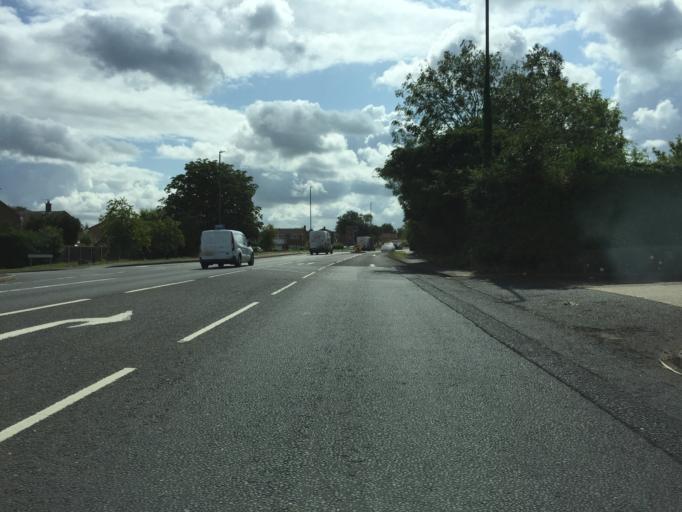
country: GB
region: England
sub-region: Kent
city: Aylesford
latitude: 51.2875
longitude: 0.4914
